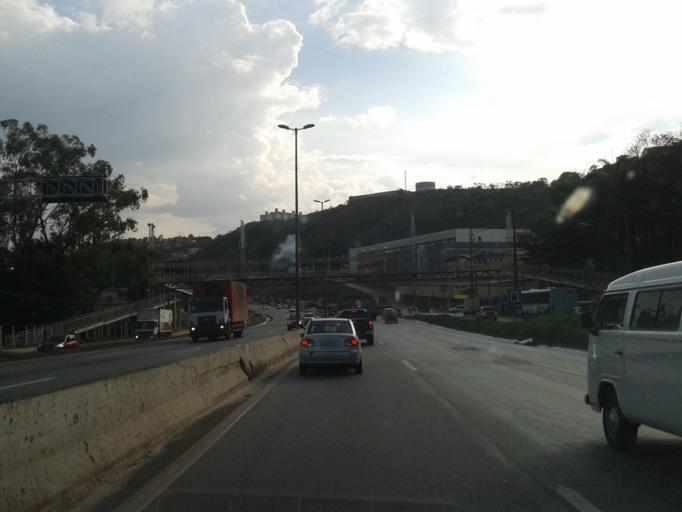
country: BR
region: Minas Gerais
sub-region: Belo Horizonte
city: Belo Horizonte
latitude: -19.8919
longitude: -43.9761
